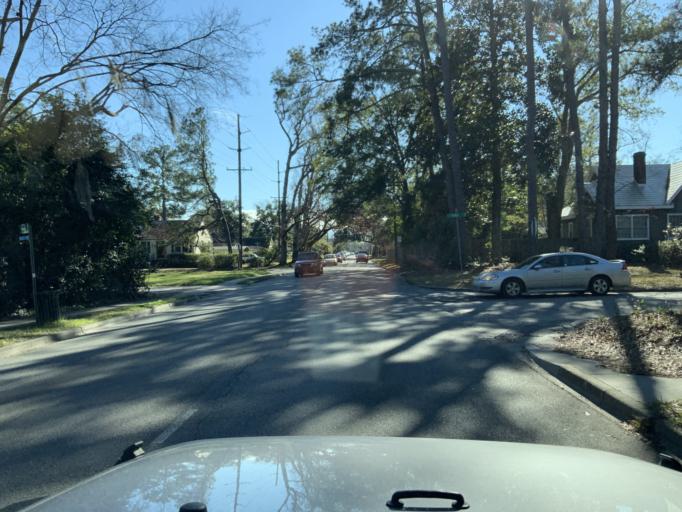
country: US
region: Georgia
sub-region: Chatham County
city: Thunderbolt
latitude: 32.0542
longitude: -81.0629
